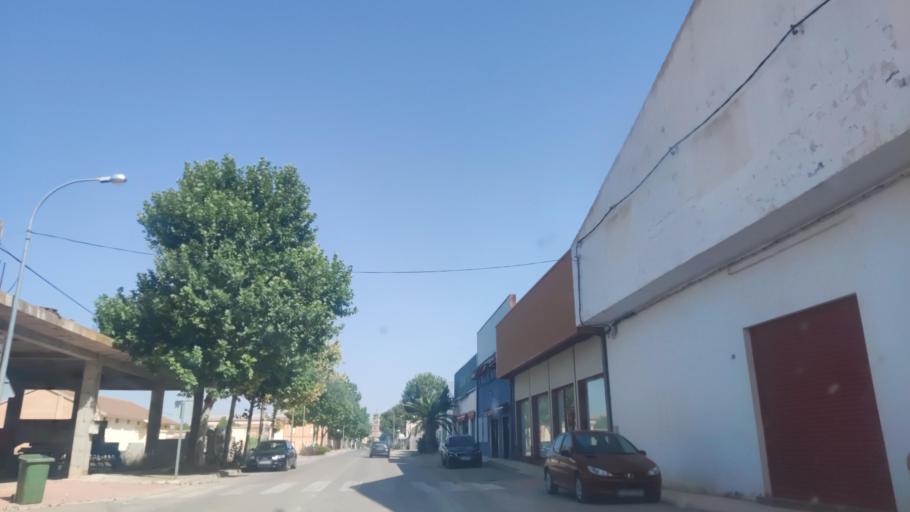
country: ES
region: Castille-La Mancha
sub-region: Provincia de Albacete
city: La Gineta
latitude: 39.1093
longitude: -1.9922
